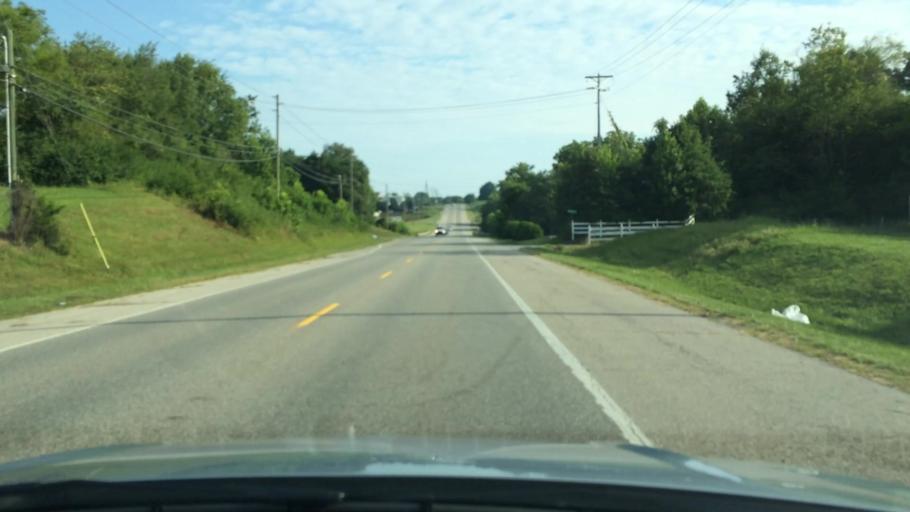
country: US
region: Tennessee
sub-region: Blount County
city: Maryville
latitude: 35.7472
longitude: -84.0443
